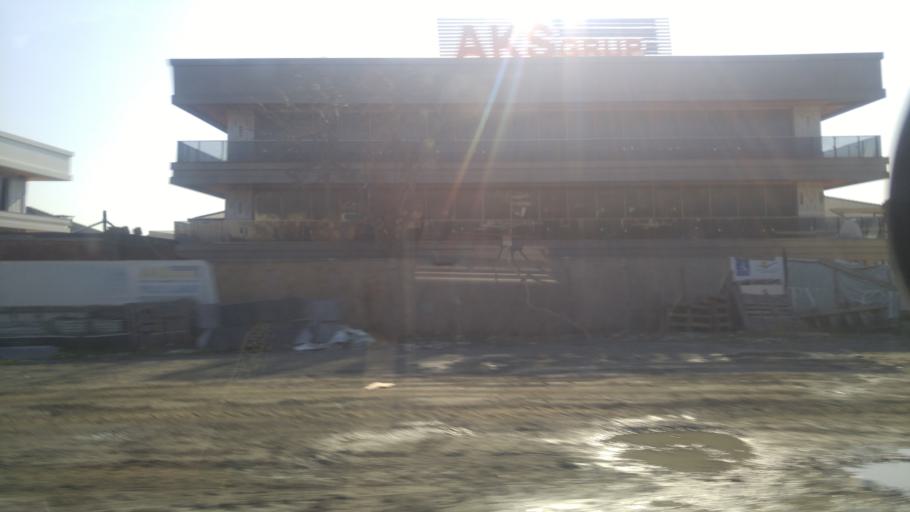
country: TR
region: Istanbul
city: Kumburgaz
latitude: 41.0163
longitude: 28.4873
